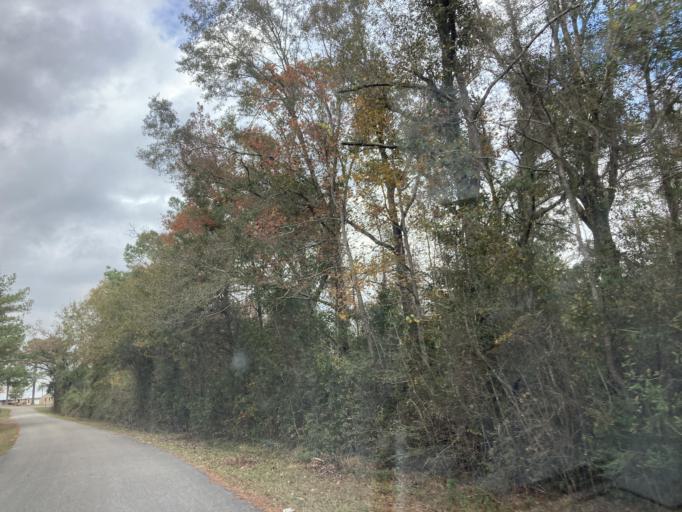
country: US
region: Mississippi
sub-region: Lamar County
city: Purvis
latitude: 31.1507
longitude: -89.5512
